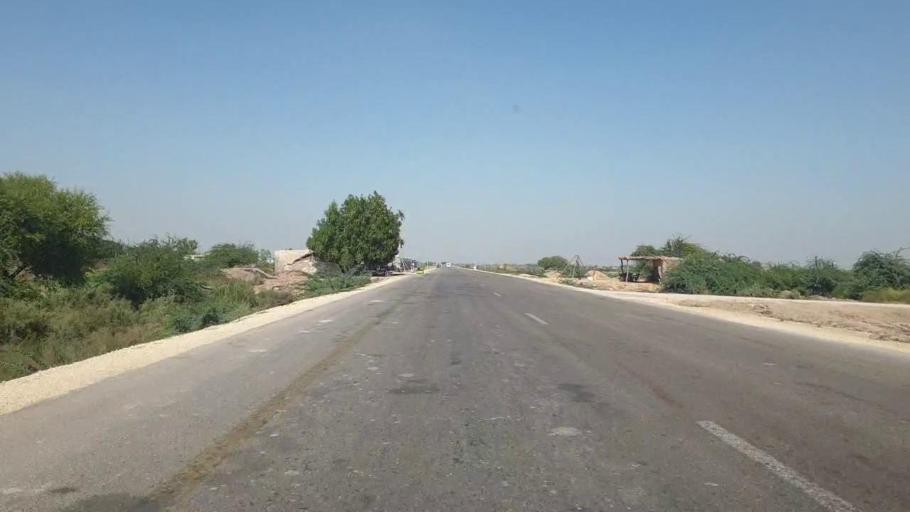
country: PK
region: Sindh
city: Talhar
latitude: 24.8325
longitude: 68.8160
